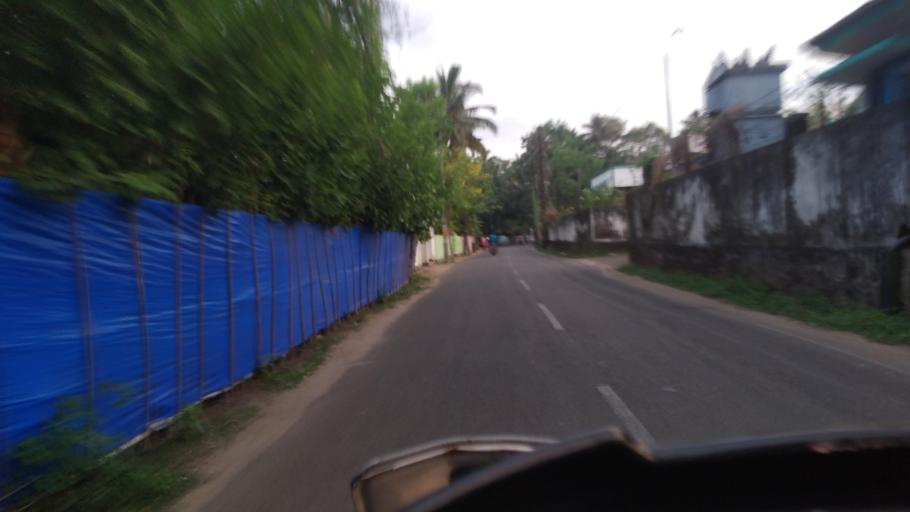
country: IN
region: Kerala
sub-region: Thrissur District
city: Kodungallur
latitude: 10.1714
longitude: 76.1984
